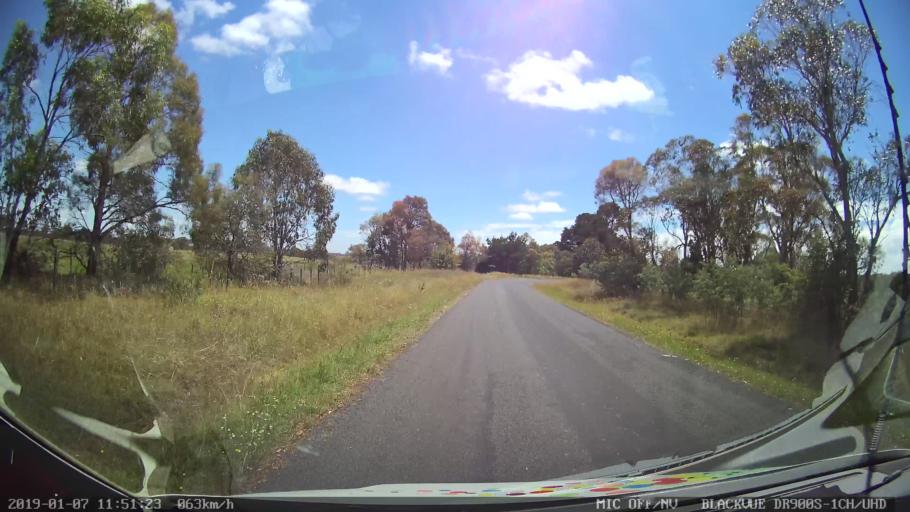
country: AU
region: New South Wales
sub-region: Guyra
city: Guyra
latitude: -30.3086
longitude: 151.6452
